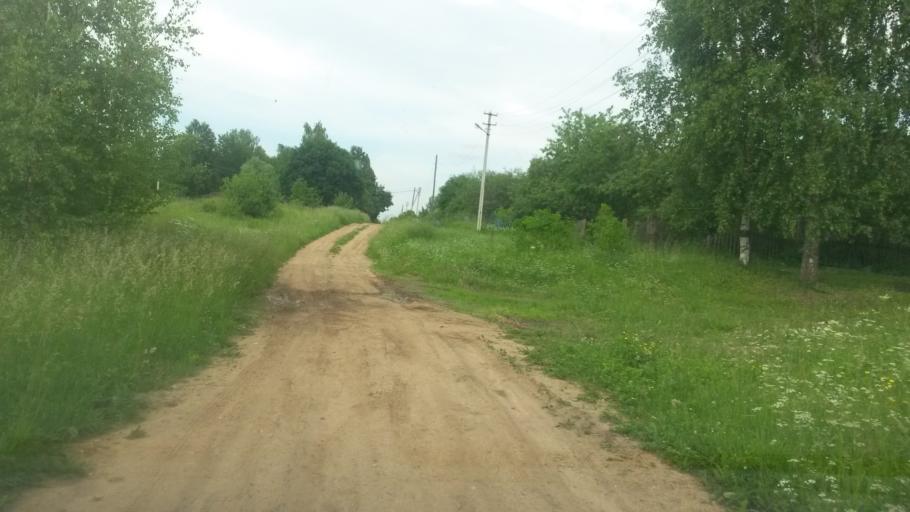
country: RU
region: Jaroslavl
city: Gavrilov-Yam
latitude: 57.3058
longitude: 39.9457
